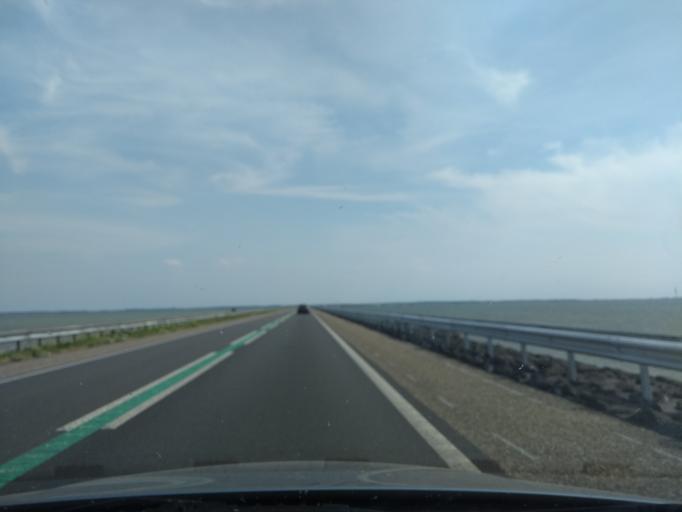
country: NL
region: Flevoland
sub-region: Gemeente Lelystad
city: Lelystad
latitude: 52.6043
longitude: 5.4450
